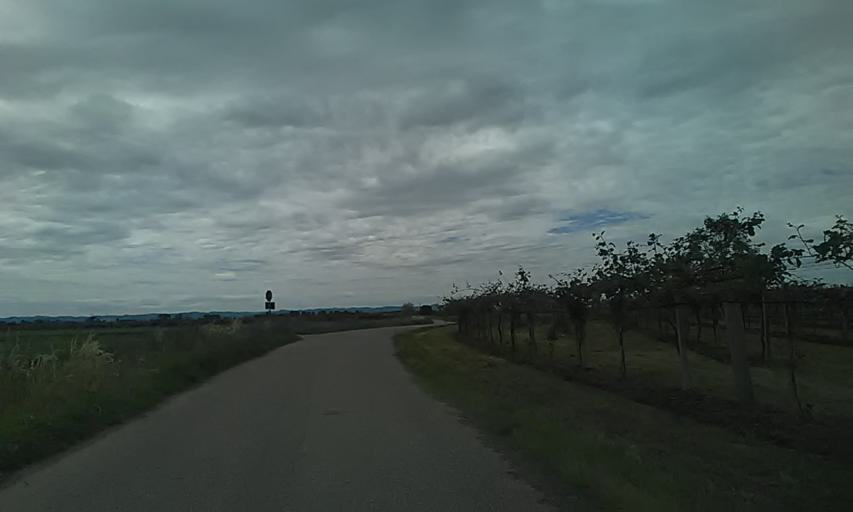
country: IT
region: Piedmont
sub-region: Provincia di Vercelli
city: Borgo d'Ale
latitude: 45.3379
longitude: 8.0517
